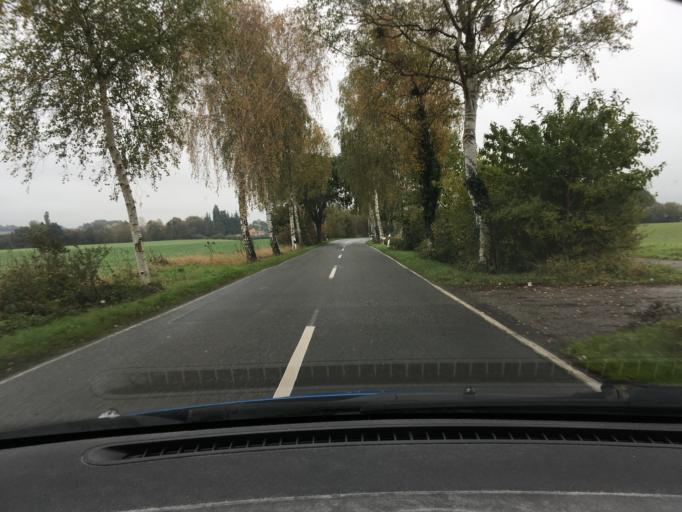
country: DE
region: Schleswig-Holstein
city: Bosau
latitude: 54.0930
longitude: 10.4690
